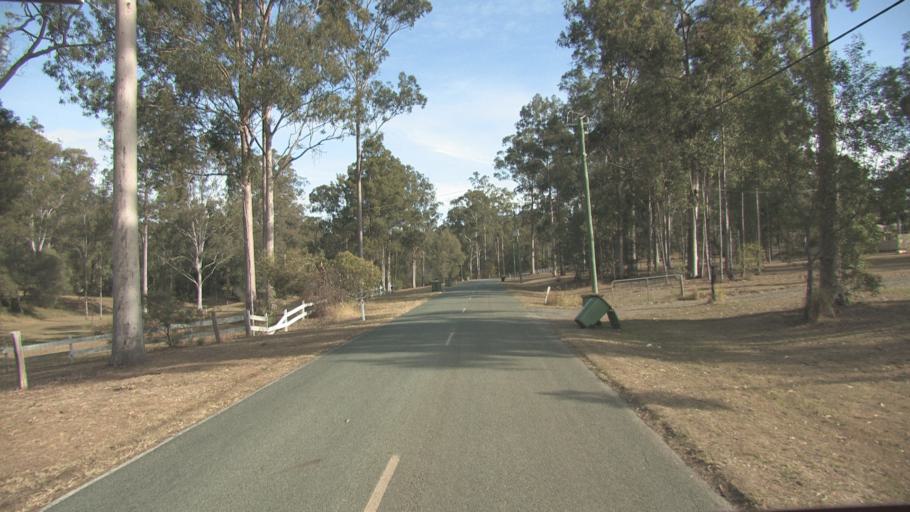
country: AU
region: Queensland
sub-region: Logan
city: Cedar Vale
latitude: -27.8784
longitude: 153.0011
